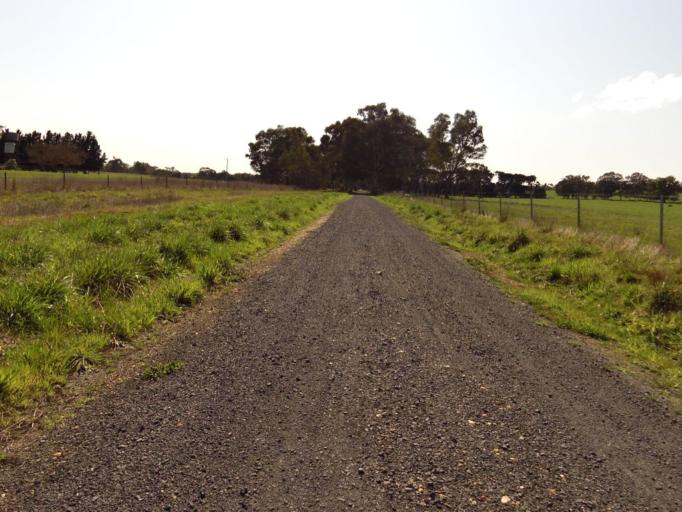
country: AU
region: Victoria
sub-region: Murrindindi
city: Alexandra
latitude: -37.1268
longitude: 145.5975
